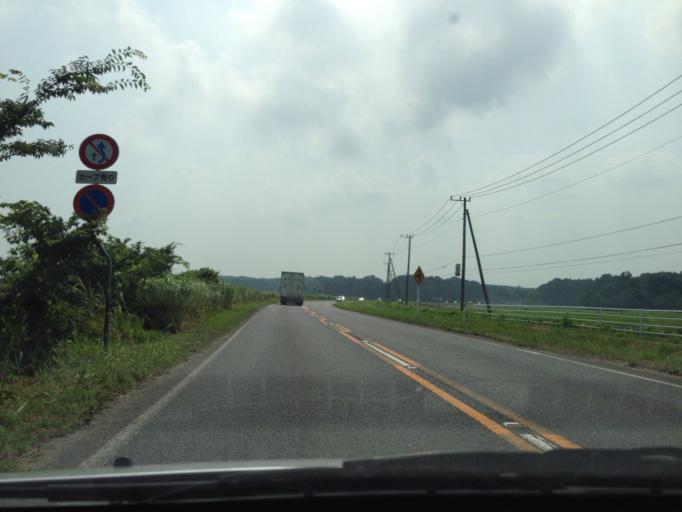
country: JP
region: Ibaraki
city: Inashiki
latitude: 36.0196
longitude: 140.2792
